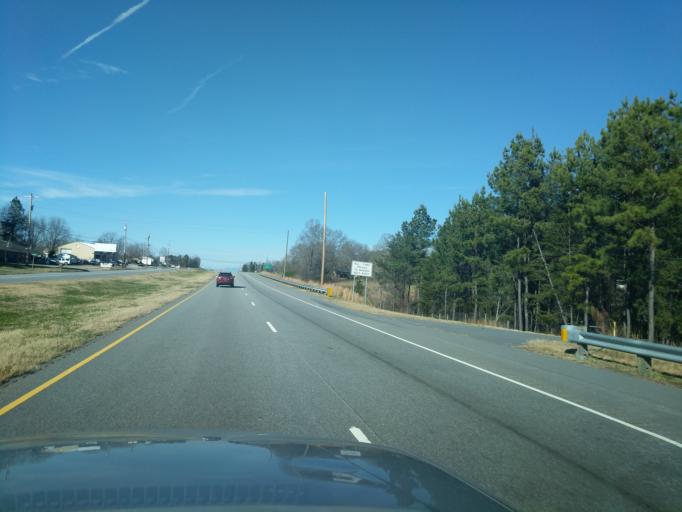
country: US
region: North Carolina
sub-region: Rutherford County
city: Forest City
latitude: 35.2909
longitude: -81.9072
